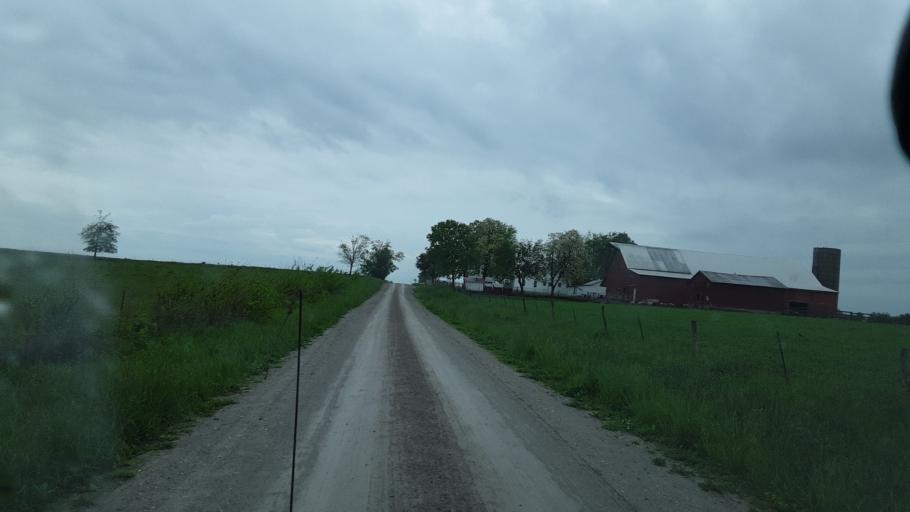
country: US
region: Missouri
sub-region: Randolph County
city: Moberly
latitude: 39.3125
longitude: -92.3049
